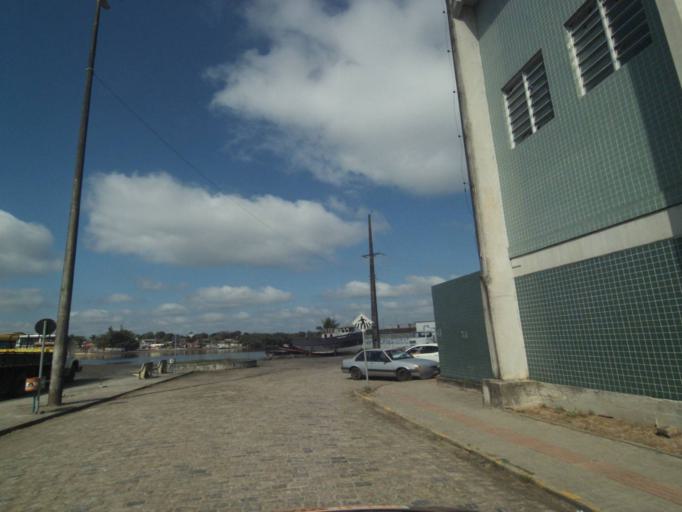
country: BR
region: Parana
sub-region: Paranagua
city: Paranagua
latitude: -25.5249
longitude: -48.5073
